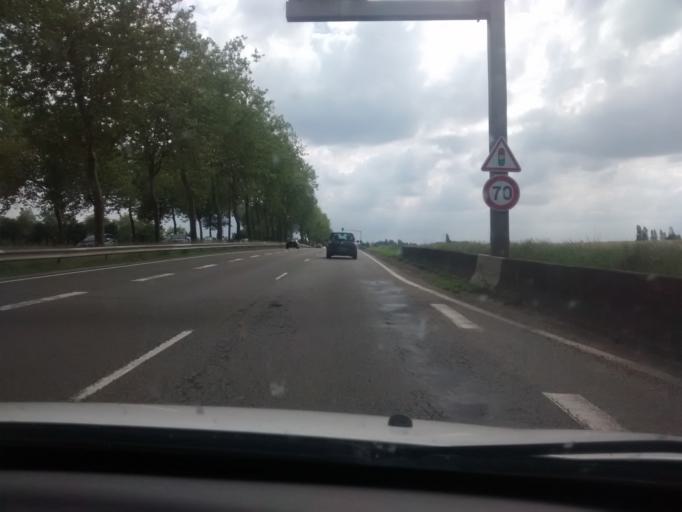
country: FR
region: Ile-de-France
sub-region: Departement des Yvelines
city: Les Essarts-le-Roi
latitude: 48.7276
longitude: 1.8948
